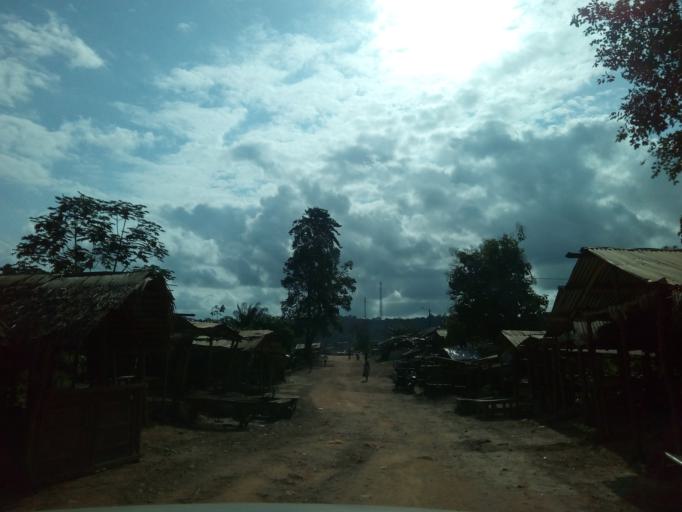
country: CI
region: Sud-Comoe
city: Mafere
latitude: 5.2916
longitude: -2.7903
